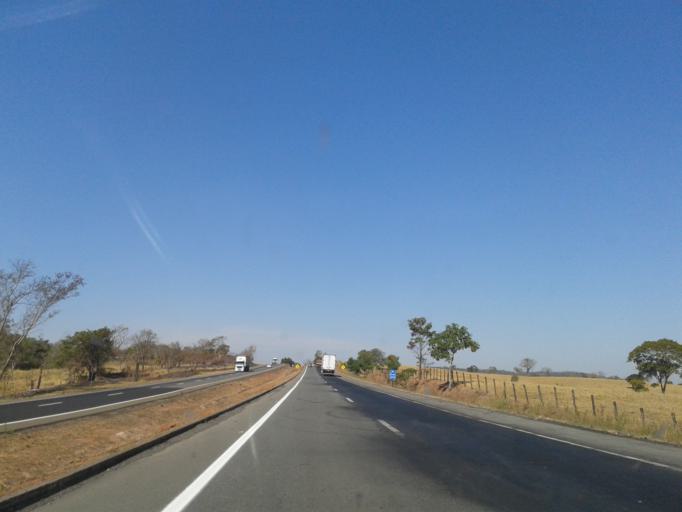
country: BR
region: Goias
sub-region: Piracanjuba
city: Piracanjuba
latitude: -17.3114
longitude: -49.2379
